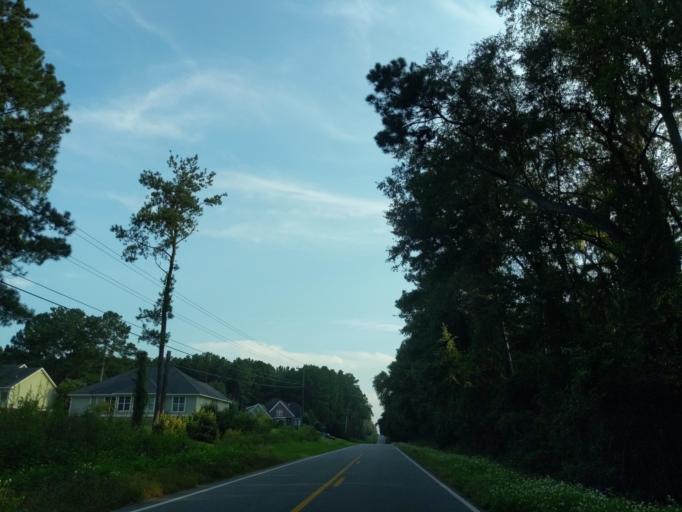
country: US
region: Georgia
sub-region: Thomas County
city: Thomasville
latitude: 30.8973
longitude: -83.9468
